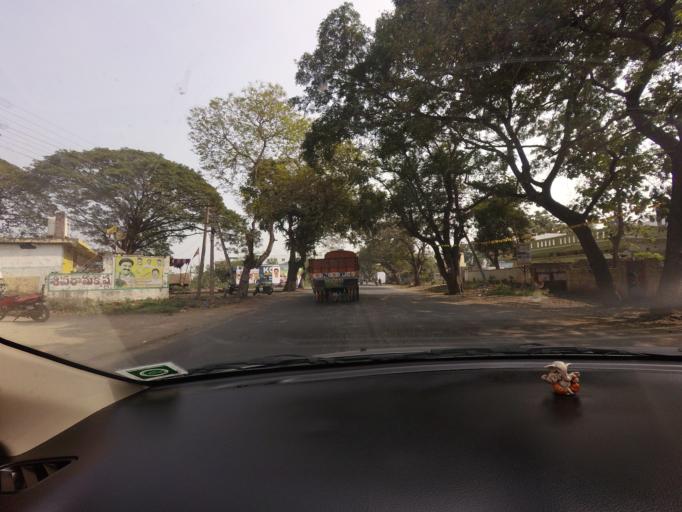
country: IN
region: Andhra Pradesh
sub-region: Krishna
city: Kankipadu
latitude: 16.4401
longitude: 80.7602
